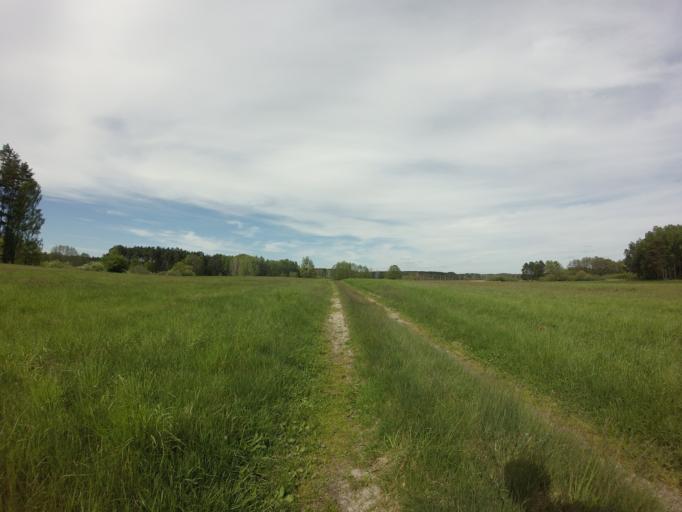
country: PL
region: West Pomeranian Voivodeship
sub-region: Powiat choszczenski
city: Drawno
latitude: 53.1577
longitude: 15.6649
